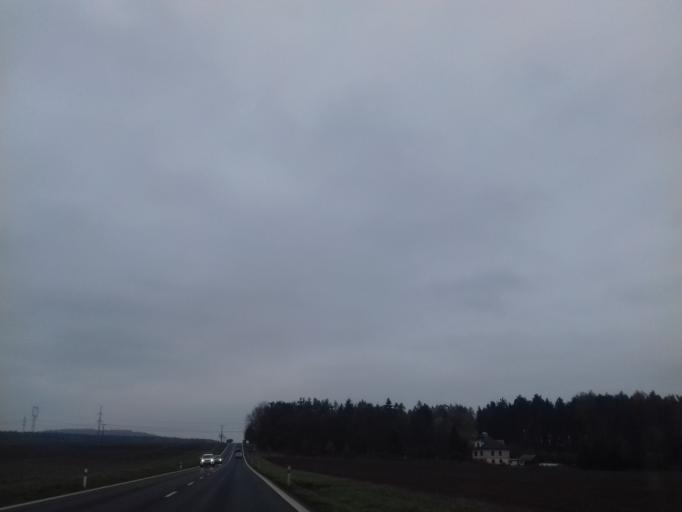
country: CZ
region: Plzensky
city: Stod
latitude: 49.6294
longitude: 13.1548
